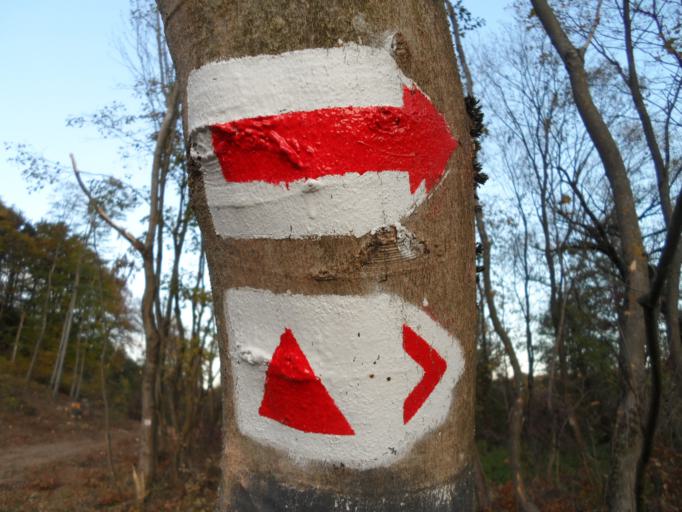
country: HU
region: Veszprem
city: Herend
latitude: 47.1116
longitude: 17.7921
